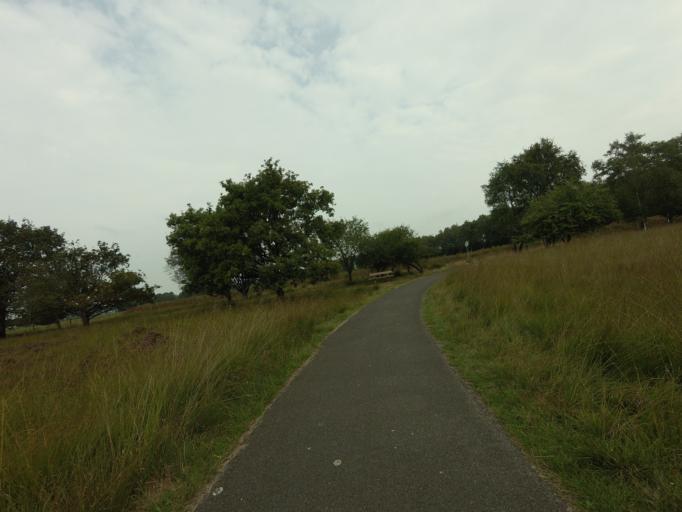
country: NL
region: Drenthe
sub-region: Gemeente Westerveld
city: Dwingeloo
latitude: 52.8837
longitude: 6.4605
